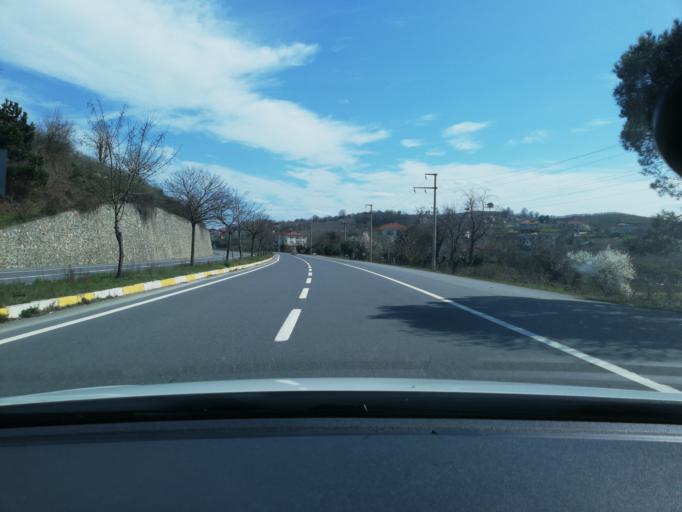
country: TR
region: Duzce
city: Akcakoca
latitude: 41.0965
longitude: 31.2161
